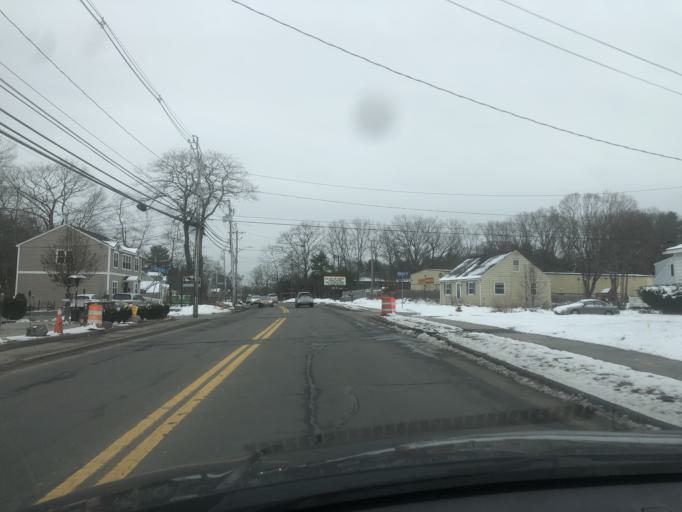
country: US
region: Massachusetts
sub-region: Middlesex County
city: Tewksbury
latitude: 42.6048
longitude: -71.2248
